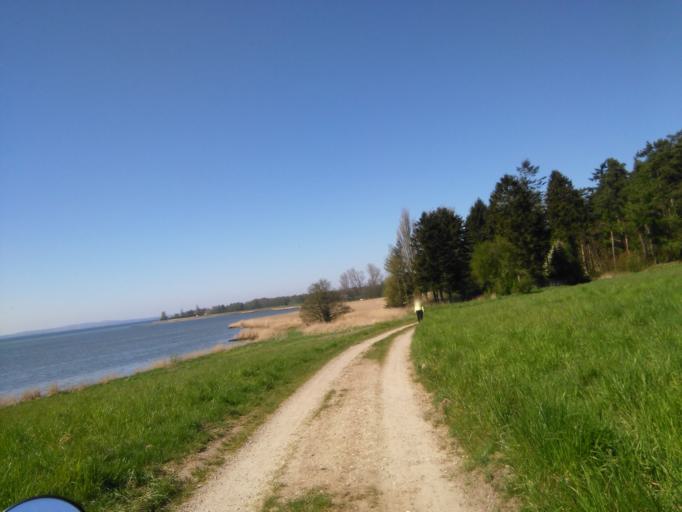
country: DK
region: Central Jutland
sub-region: Odder Kommune
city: Odder
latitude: 55.8851
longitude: 10.0793
